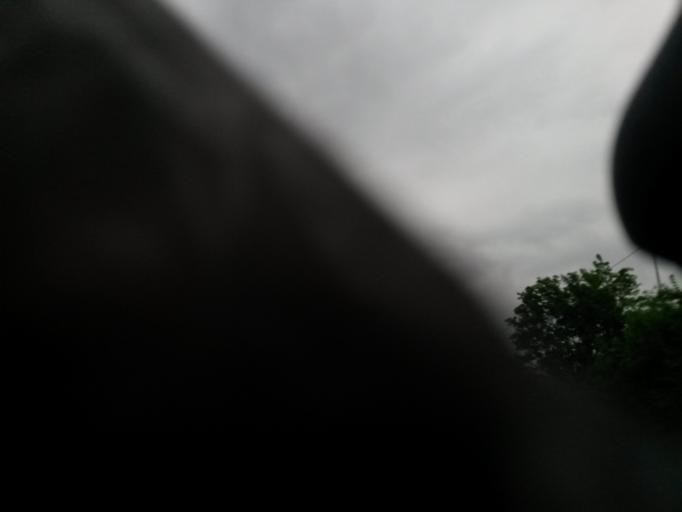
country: DE
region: Baden-Wuerttemberg
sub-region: Regierungsbezirk Stuttgart
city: Ostfildern
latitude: 48.7583
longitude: 9.2586
